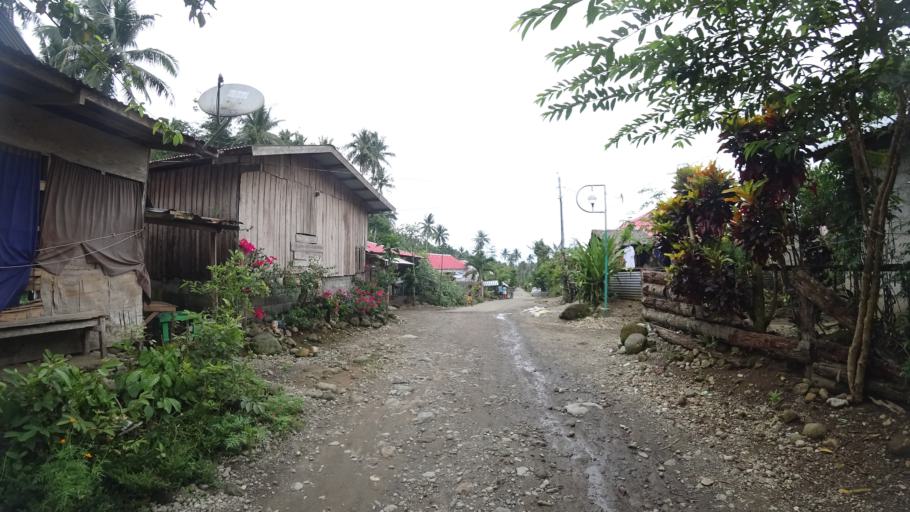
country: PH
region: Eastern Visayas
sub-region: Province of Leyte
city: Bugho
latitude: 10.8283
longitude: 124.8907
